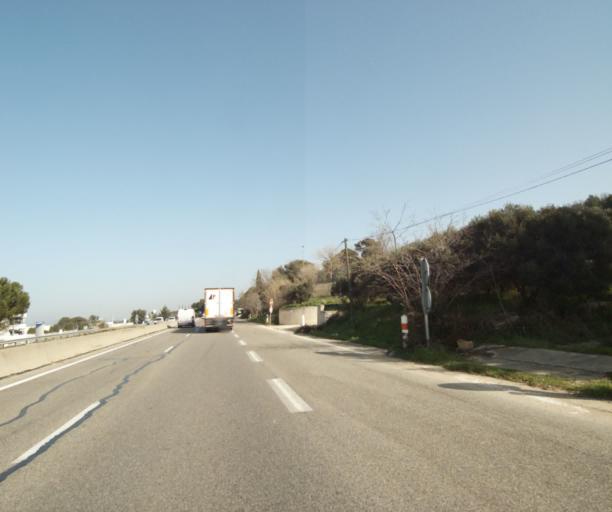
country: FR
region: Provence-Alpes-Cote d'Azur
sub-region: Departement des Bouches-du-Rhone
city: Saint-Victoret
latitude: 43.4349
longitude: 5.2353
